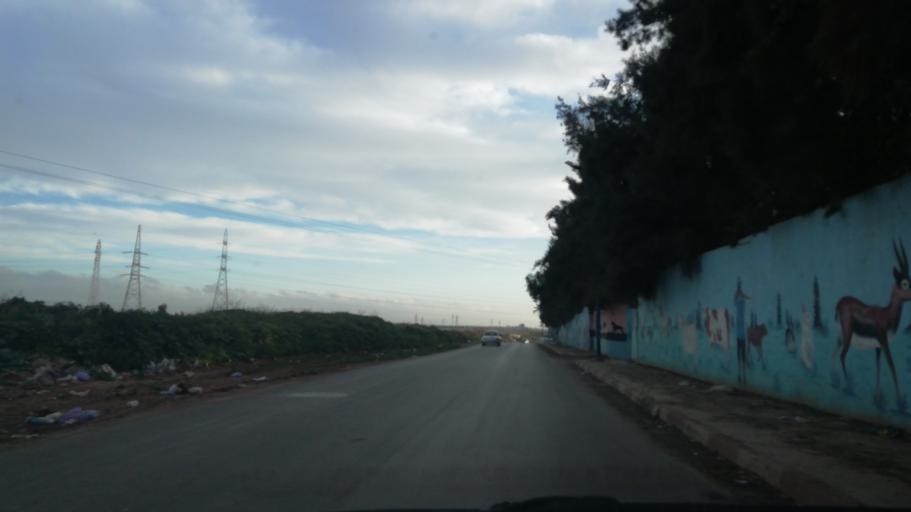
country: DZ
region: Oran
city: Es Senia
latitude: 35.6802
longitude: -0.5863
